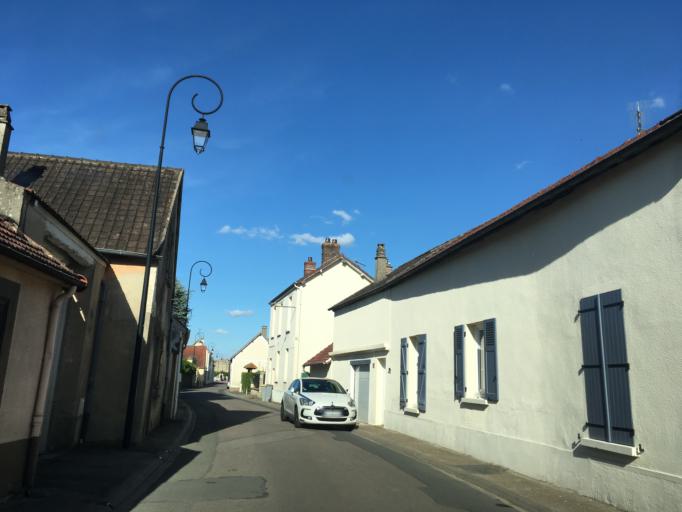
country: FR
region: Haute-Normandie
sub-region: Departement de l'Eure
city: Gasny
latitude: 49.0879
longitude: 1.6000
